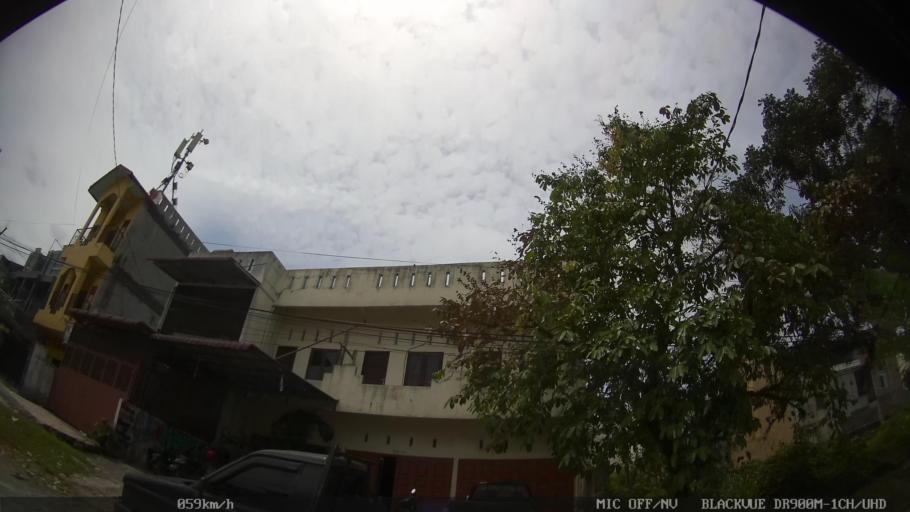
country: ID
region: North Sumatra
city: Sunggal
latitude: 3.5551
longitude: 98.6411
